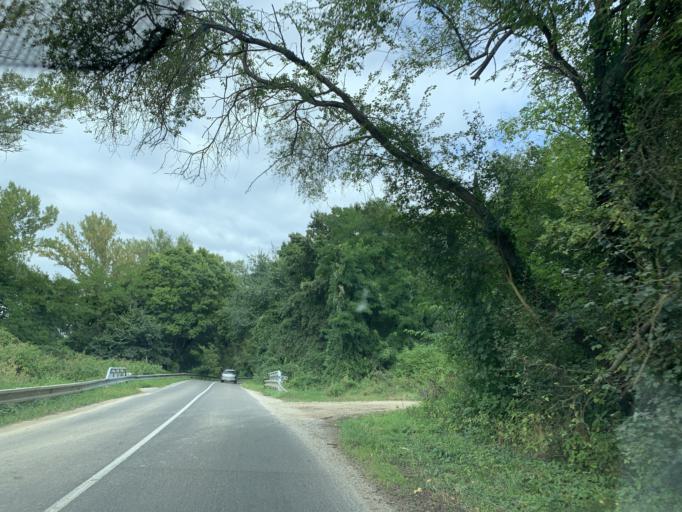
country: SK
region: Trenciansky
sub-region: Okres Nove Mesto nad Vahom
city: Nove Mesto nad Vahom
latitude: 48.8112
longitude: 17.9201
